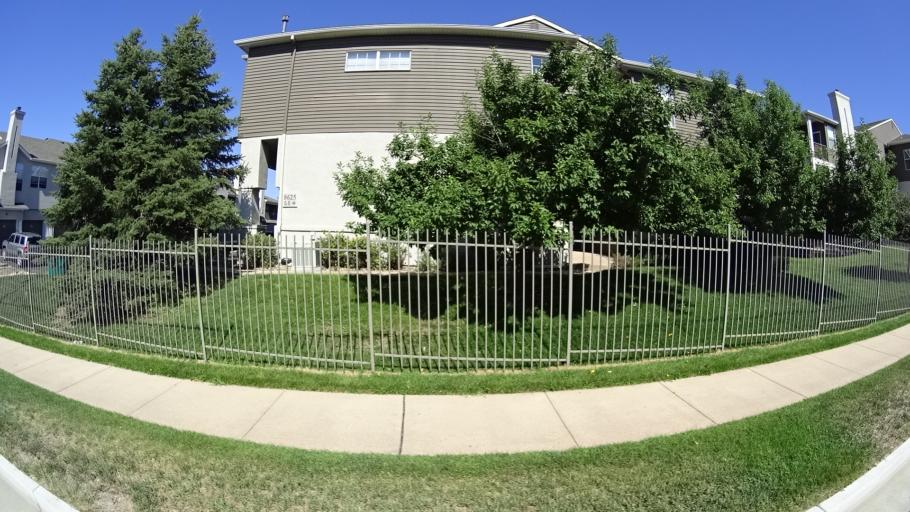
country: US
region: Colorado
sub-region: El Paso County
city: Black Forest
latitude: 38.9549
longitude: -104.7705
